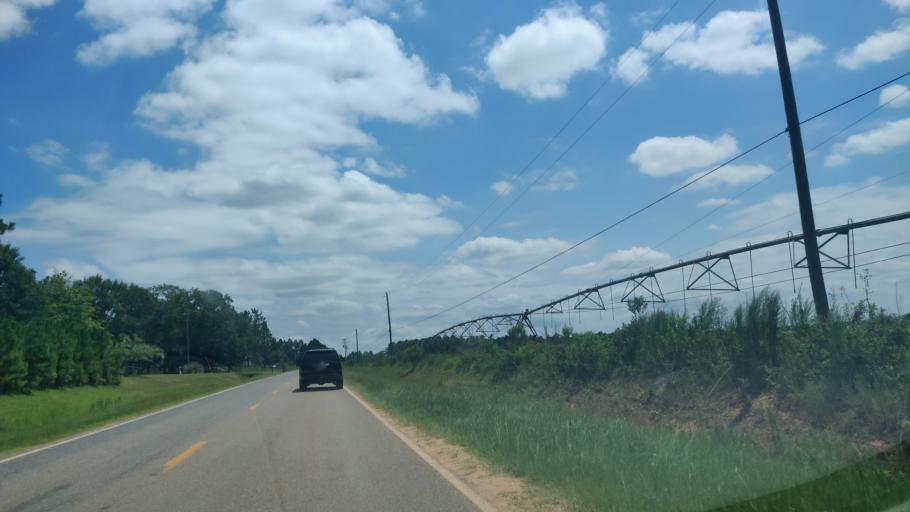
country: US
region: Georgia
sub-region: Tift County
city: Omega
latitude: 31.4323
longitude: -83.6375
